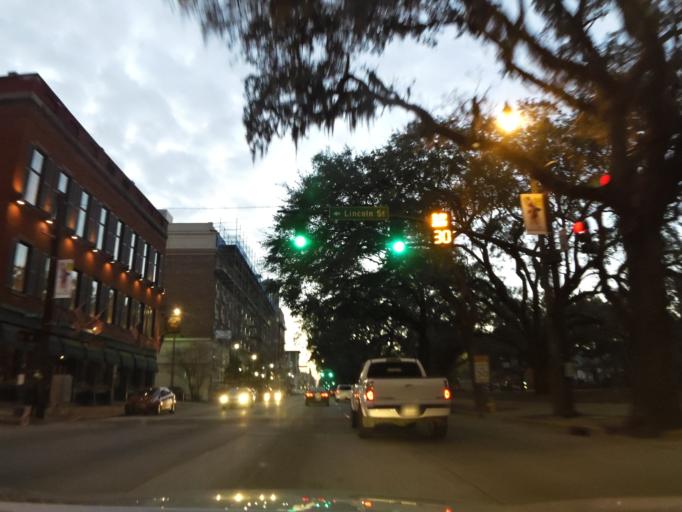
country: US
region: Georgia
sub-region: Chatham County
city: Savannah
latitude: 32.0800
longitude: -81.0876
